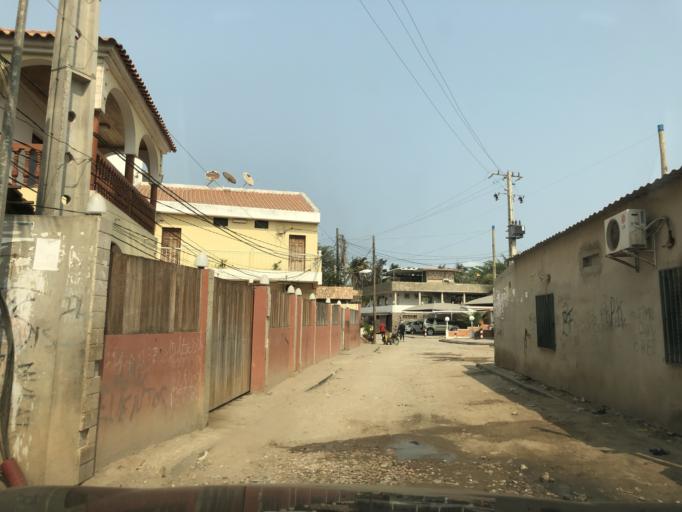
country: AO
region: Luanda
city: Luanda
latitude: -8.9033
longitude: 13.1647
